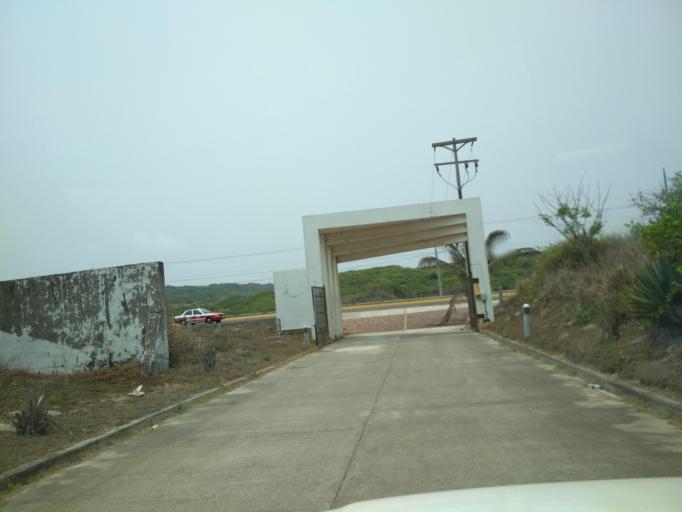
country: MX
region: Veracruz
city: Anton Lizardo
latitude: 19.0553
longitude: -96.0436
